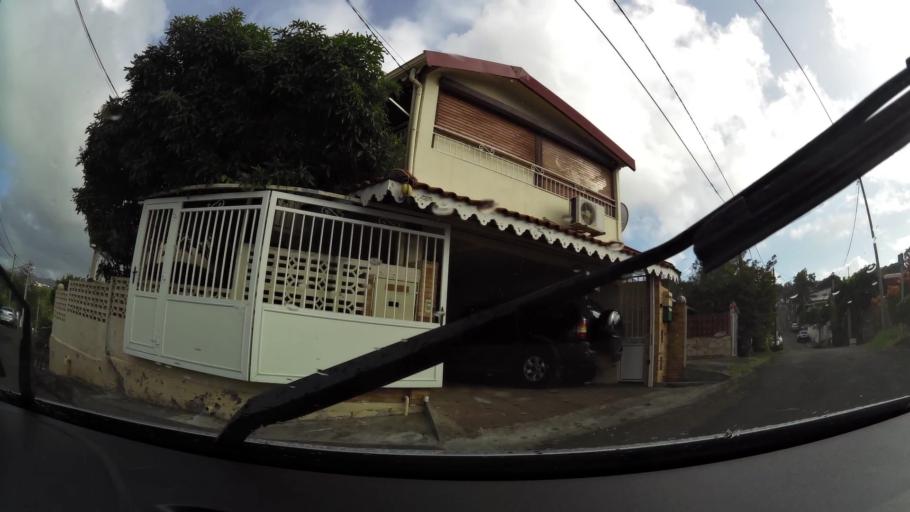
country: MQ
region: Martinique
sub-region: Martinique
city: Ducos
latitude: 14.5796
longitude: -60.9804
